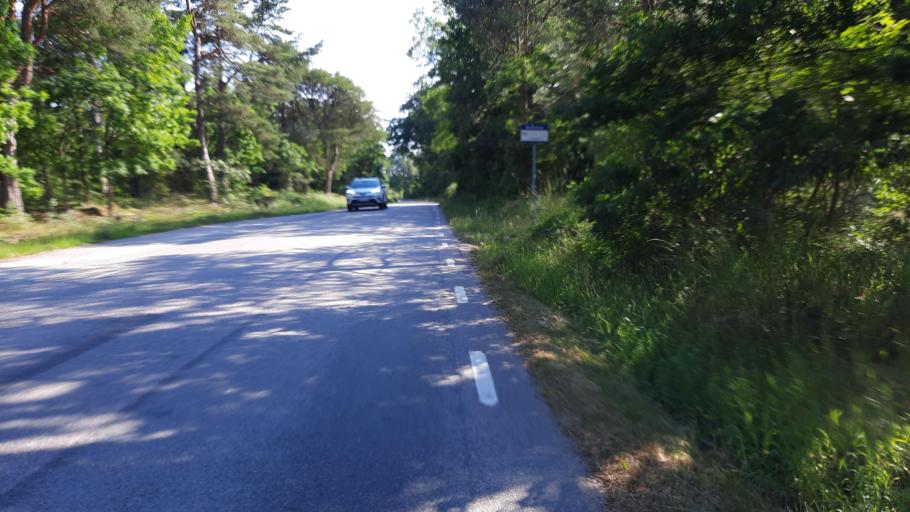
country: SE
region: Blekinge
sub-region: Karlskrona Kommun
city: Sturko
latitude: 56.0949
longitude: 15.6942
